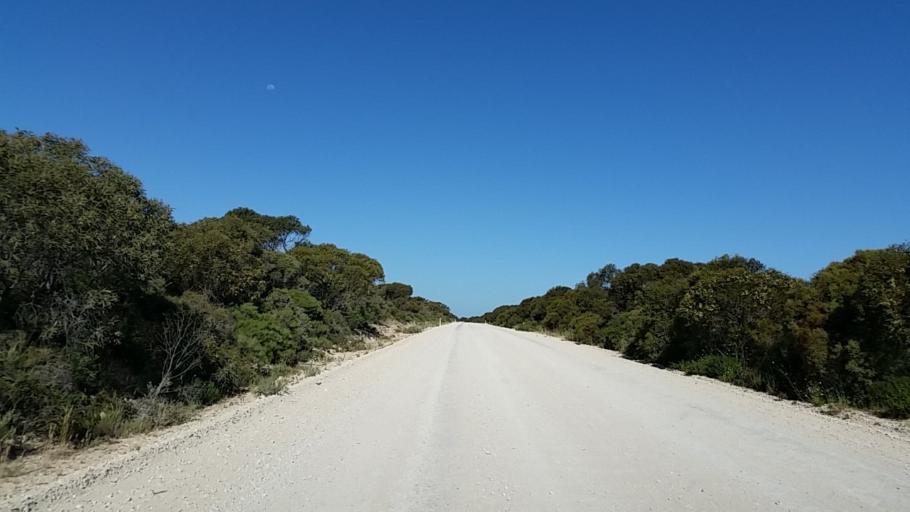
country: AU
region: South Australia
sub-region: Yorke Peninsula
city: Honiton
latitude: -35.2154
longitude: 137.0163
